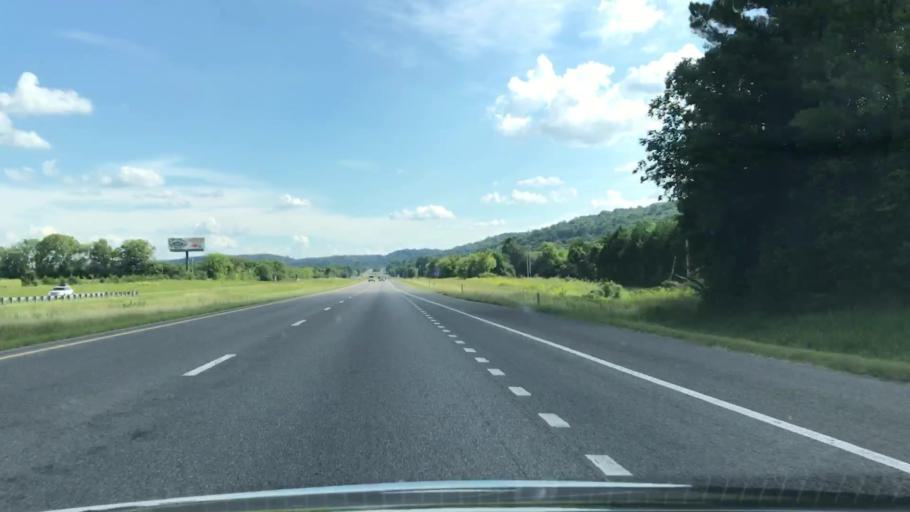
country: US
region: Tennessee
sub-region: Marshall County
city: Cornersville
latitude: 35.4438
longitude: -86.8830
